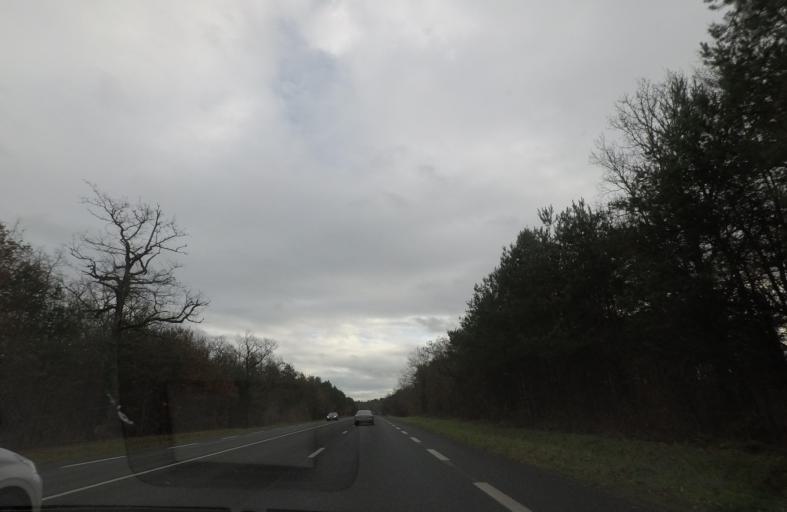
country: FR
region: Centre
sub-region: Departement du Loir-et-Cher
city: Mur-de-Sologne
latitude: 47.3953
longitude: 1.6452
